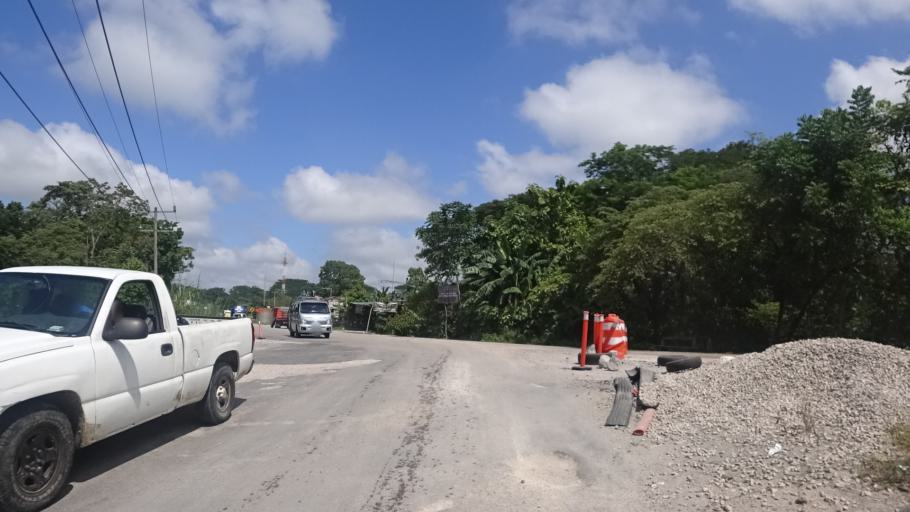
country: MX
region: Chiapas
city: Palenque
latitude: 17.4925
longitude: -91.9837
